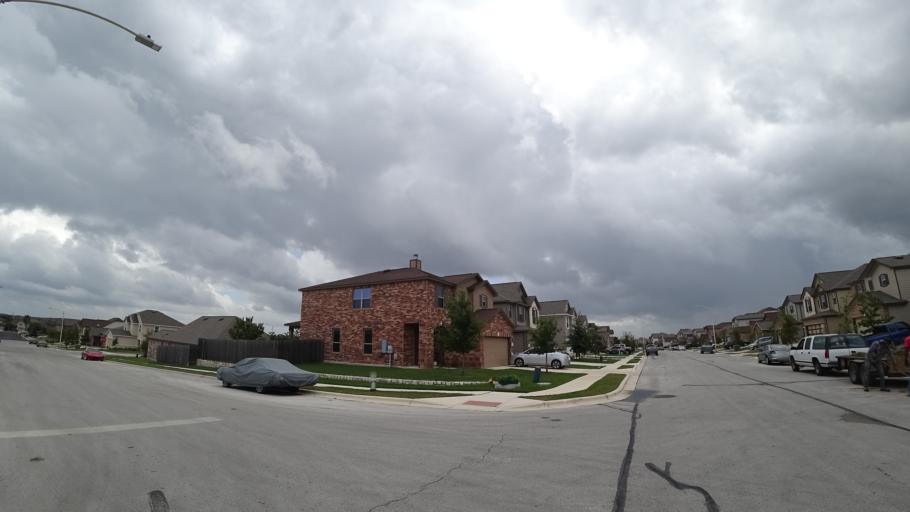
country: US
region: Texas
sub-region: Travis County
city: Onion Creek
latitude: 30.1478
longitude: -97.7439
